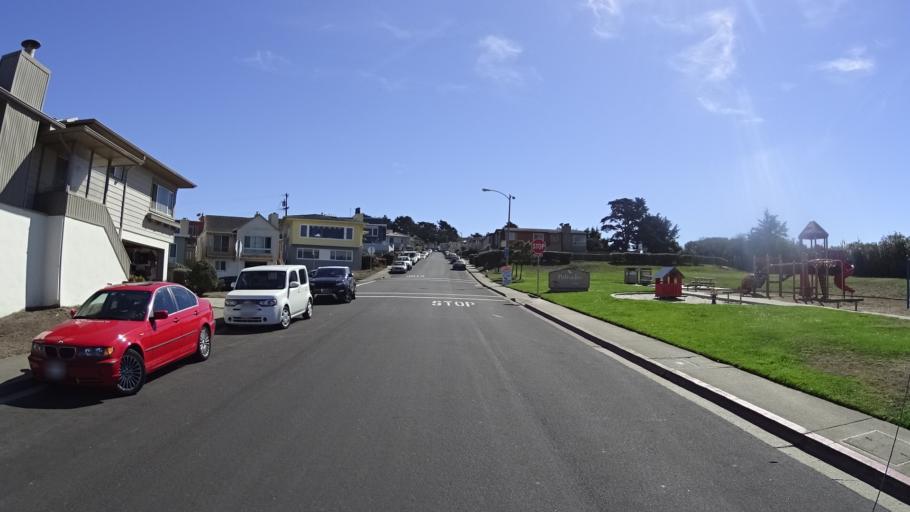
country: US
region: California
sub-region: San Mateo County
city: Broadmoor
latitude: 37.6893
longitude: -122.4950
